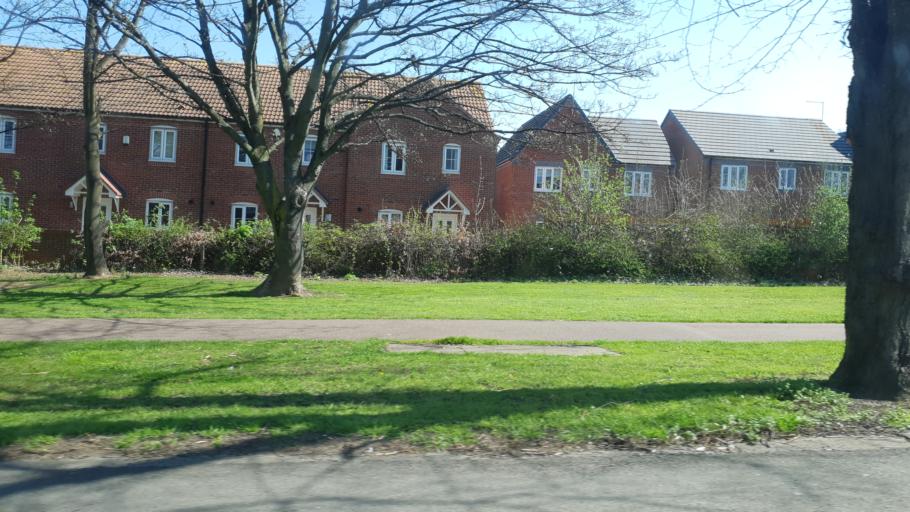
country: GB
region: England
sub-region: Middlesbrough
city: Nunthorpe
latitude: 54.5455
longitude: -1.2144
